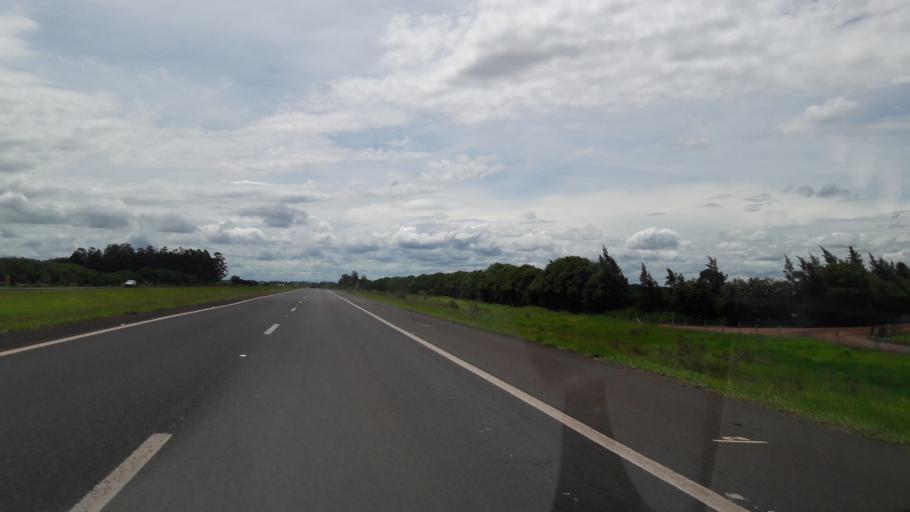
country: BR
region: Sao Paulo
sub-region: Avare
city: Avare
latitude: -22.9319
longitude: -49.0027
